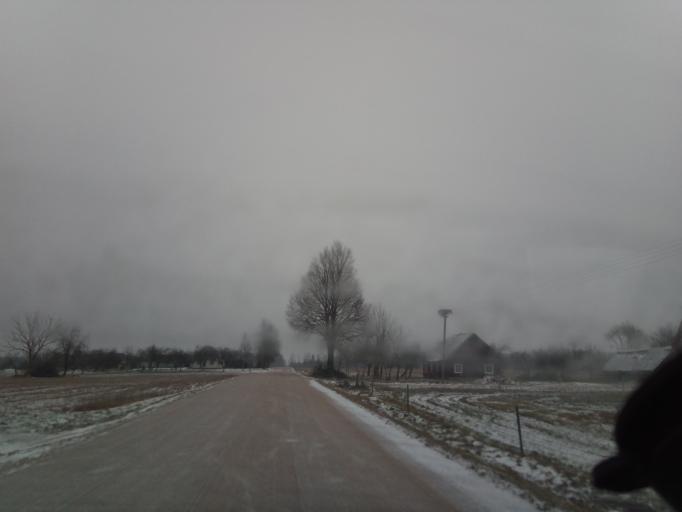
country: LT
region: Utenos apskritis
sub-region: Anyksciai
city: Anyksciai
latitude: 55.4460
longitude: 25.1032
